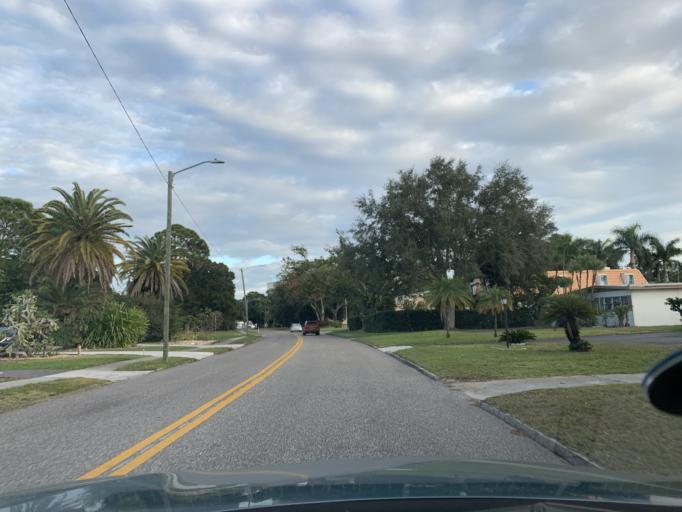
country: US
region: Florida
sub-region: Pinellas County
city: South Pasadena
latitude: 27.7637
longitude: -82.7376
